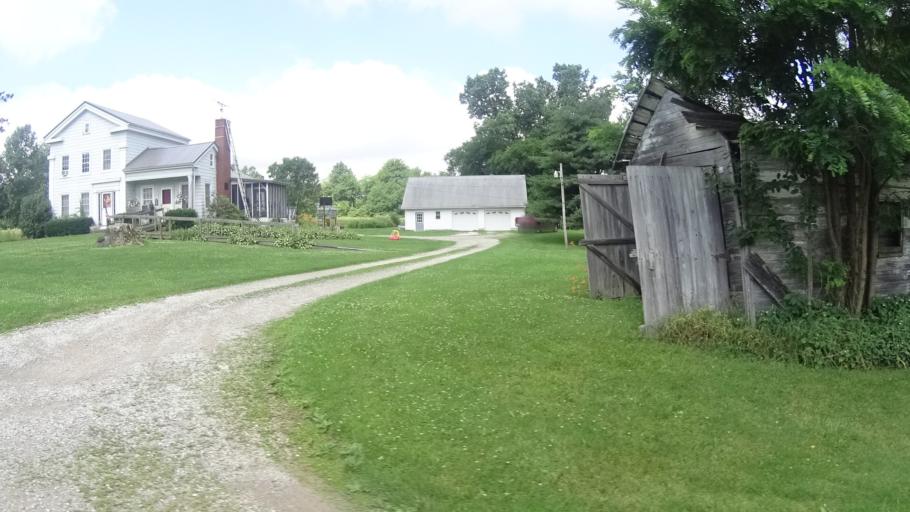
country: US
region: Ohio
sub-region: Huron County
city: Wakeman
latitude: 41.2919
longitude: -82.4202
